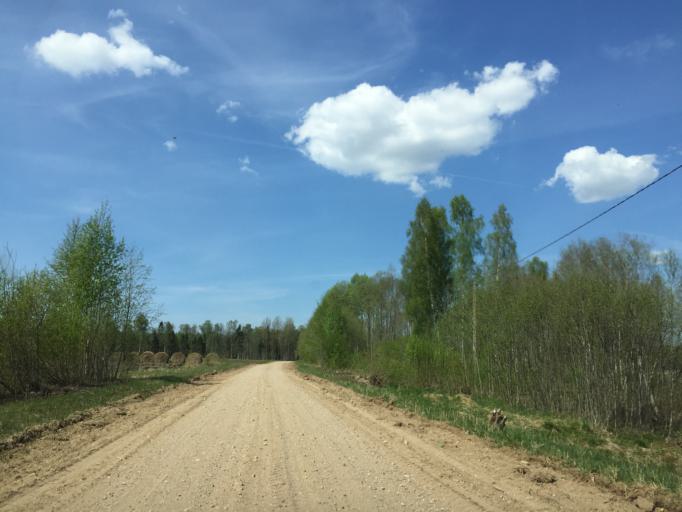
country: LV
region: Limbazu Rajons
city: Limbazi
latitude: 57.3848
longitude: 24.6081
